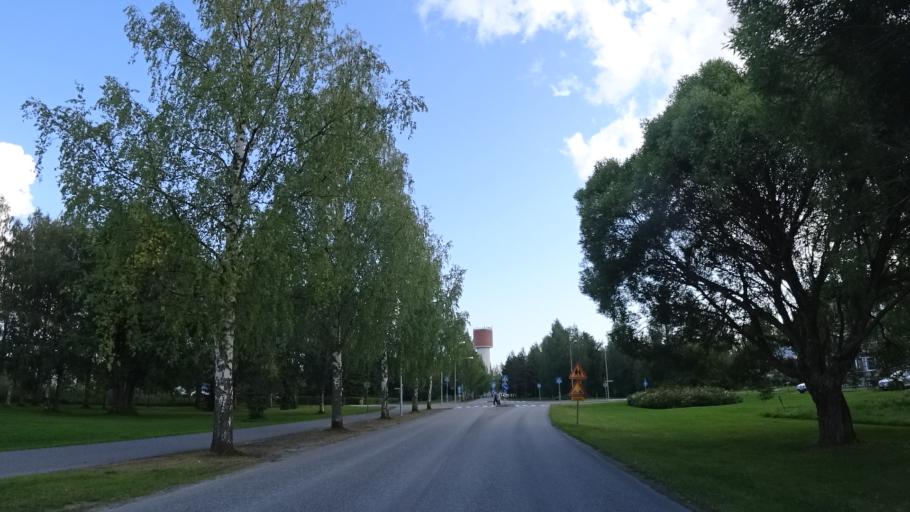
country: FI
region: North Karelia
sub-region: Pielisen Karjala
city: Lieksa
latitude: 63.3249
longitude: 30.0226
